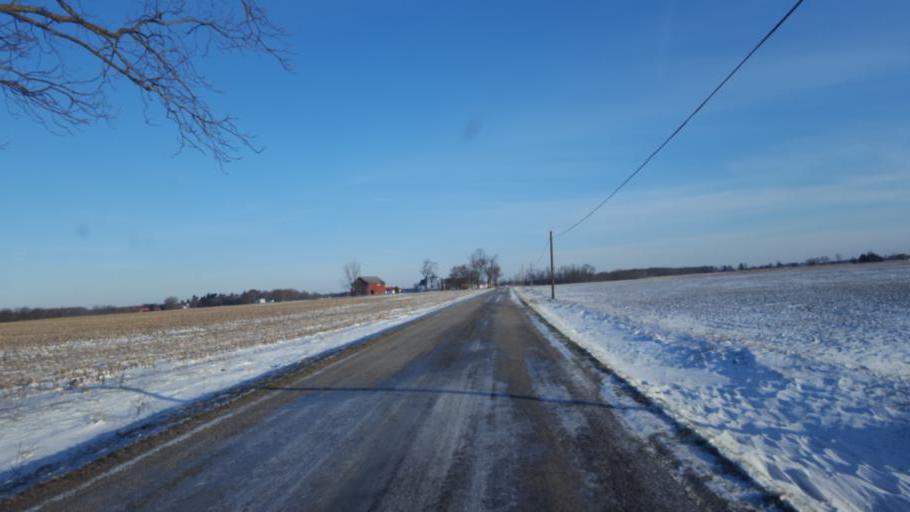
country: US
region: Ohio
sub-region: Morrow County
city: Cardington
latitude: 40.5207
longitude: -82.9028
